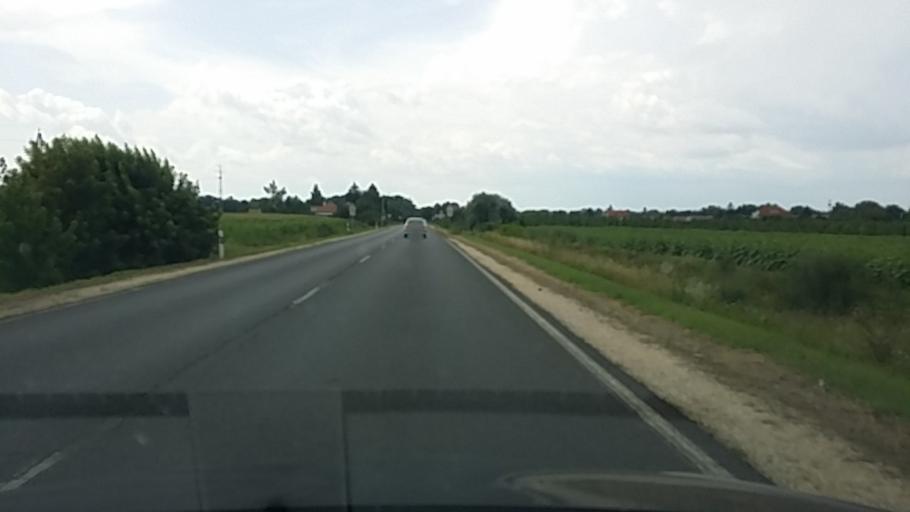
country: HU
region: Pest
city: Orkeny
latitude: 47.1200
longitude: 19.4408
